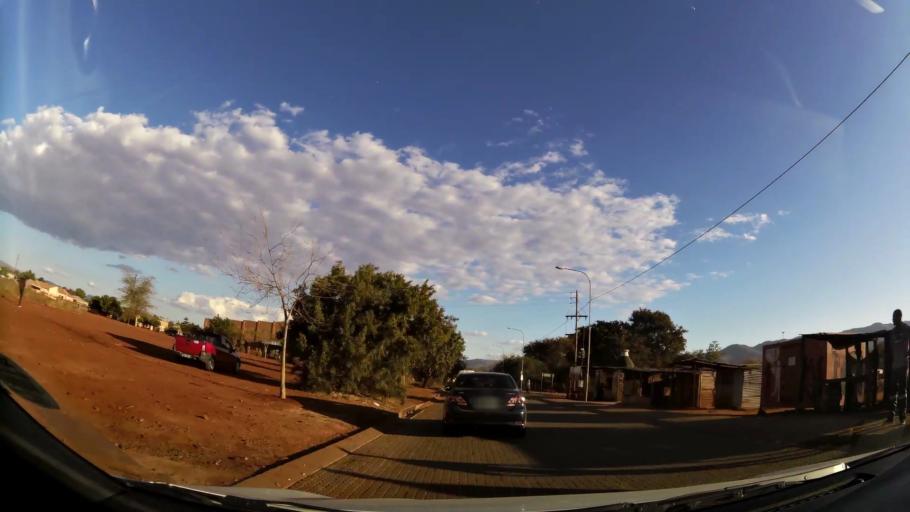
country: ZA
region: Limpopo
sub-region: Waterberg District Municipality
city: Mokopane
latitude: -24.1558
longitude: 28.9891
